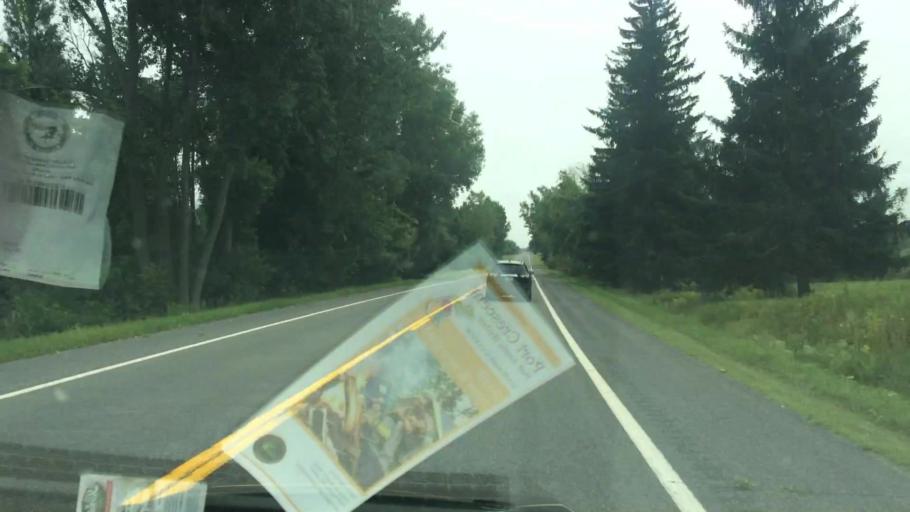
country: US
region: Michigan
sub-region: Huron County
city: Harbor Beach
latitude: 44.0191
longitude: -82.8058
